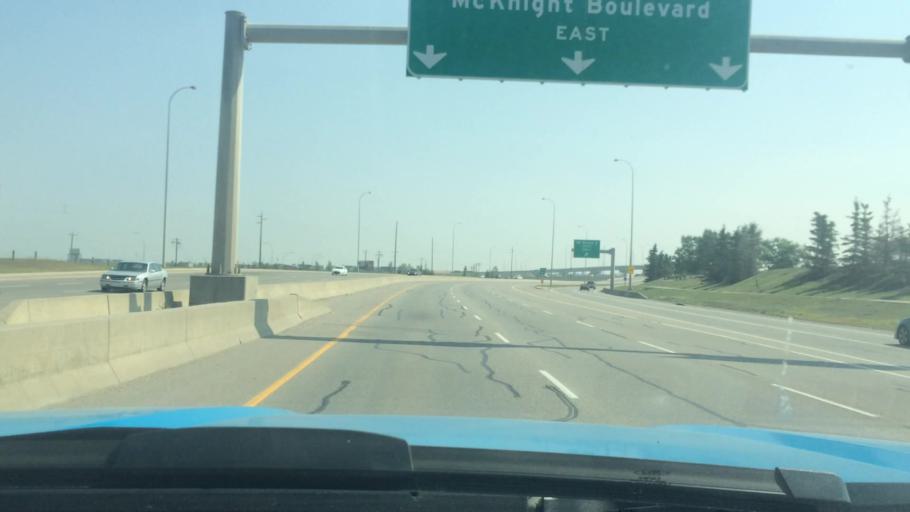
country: CA
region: Alberta
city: Calgary
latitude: 51.0947
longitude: -113.9925
